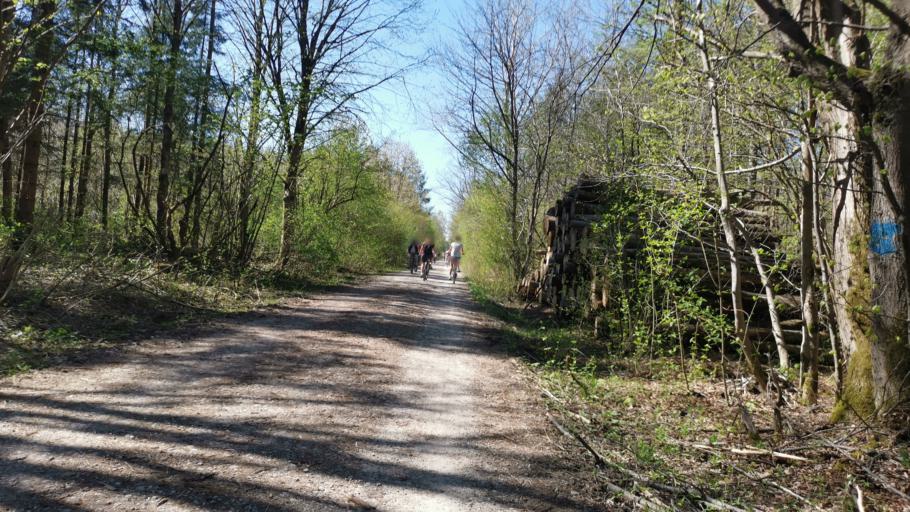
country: DE
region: Bavaria
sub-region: Upper Bavaria
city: Planegg
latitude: 48.0886
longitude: 11.4395
